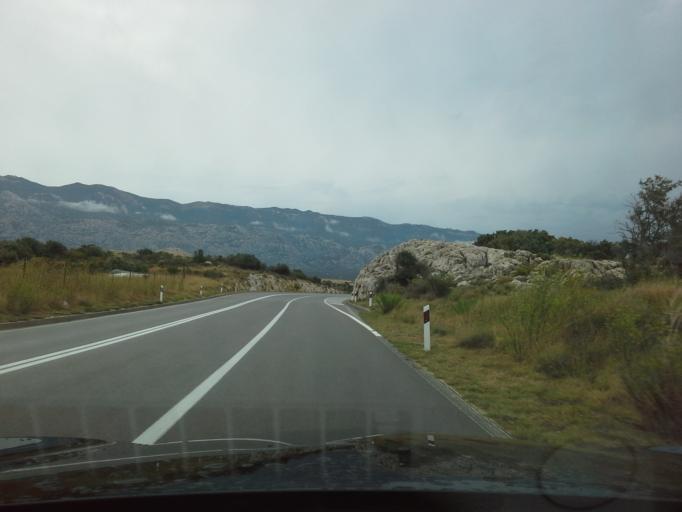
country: HR
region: Primorsko-Goranska
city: Banjol
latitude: 44.7059
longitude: 14.8417
